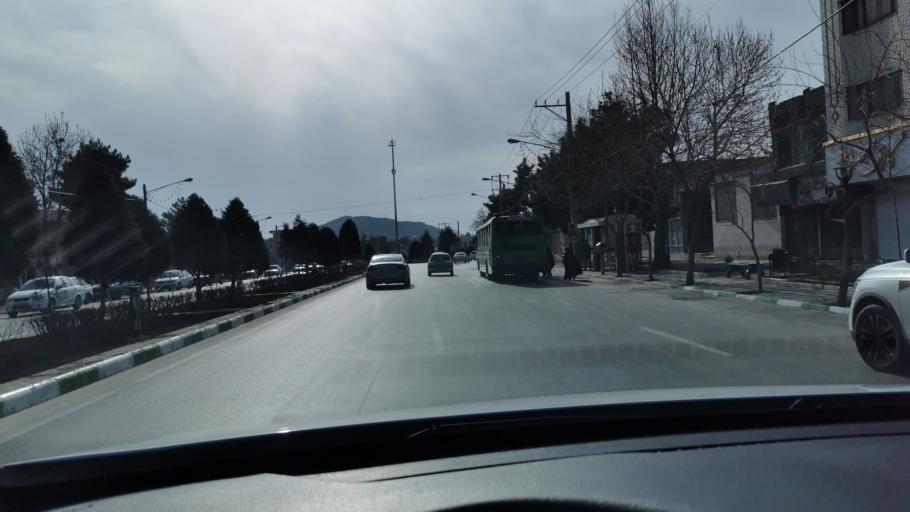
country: IR
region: Razavi Khorasan
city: Mashhad
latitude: 36.2851
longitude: 59.5476
